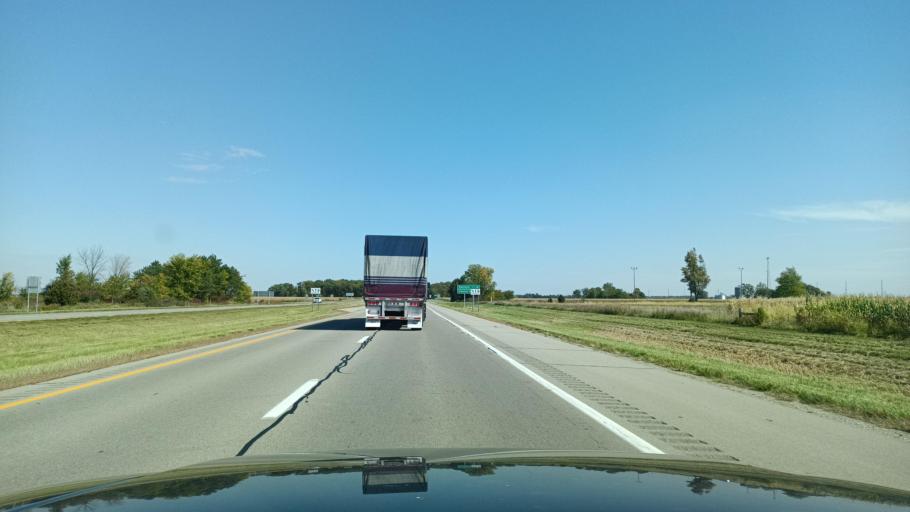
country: US
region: Ohio
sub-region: Henry County
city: Napoleon
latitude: 41.3581
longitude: -84.2235
